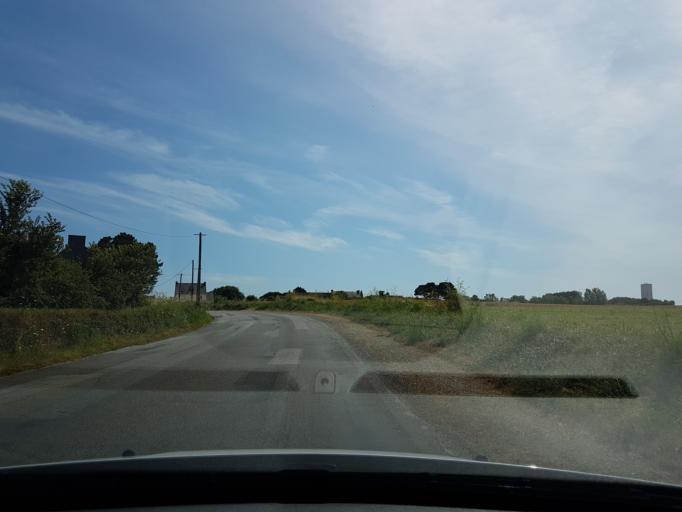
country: FR
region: Brittany
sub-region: Departement du Morbihan
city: Etel
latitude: 47.6732
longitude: -3.2208
